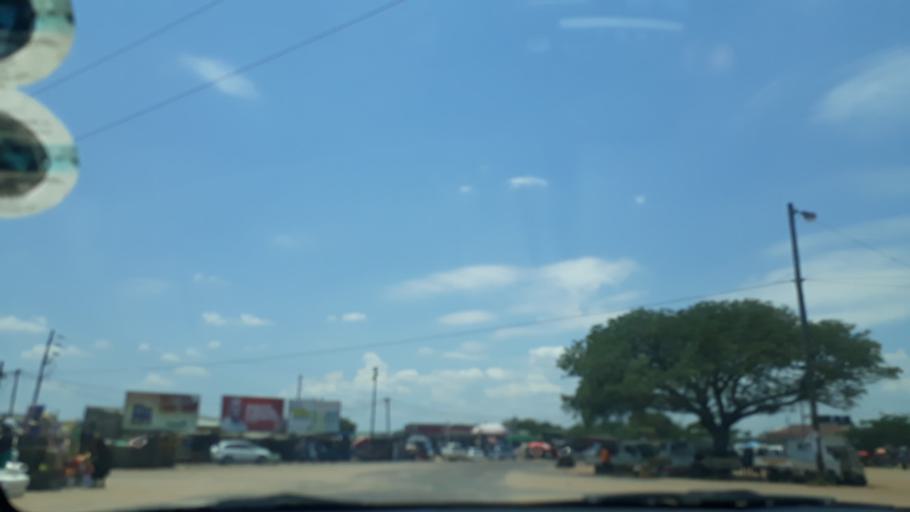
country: MZ
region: Maputo City
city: Maputo
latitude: -25.8829
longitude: 32.6042
